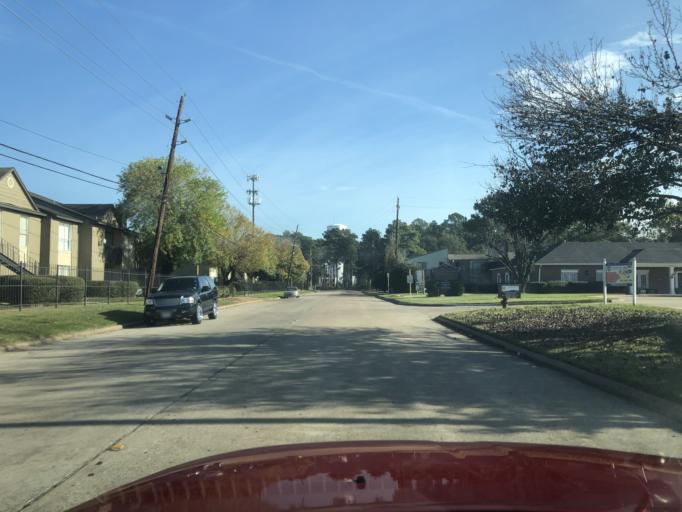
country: US
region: Texas
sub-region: Harris County
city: Spring
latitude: 30.0029
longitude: -95.4587
